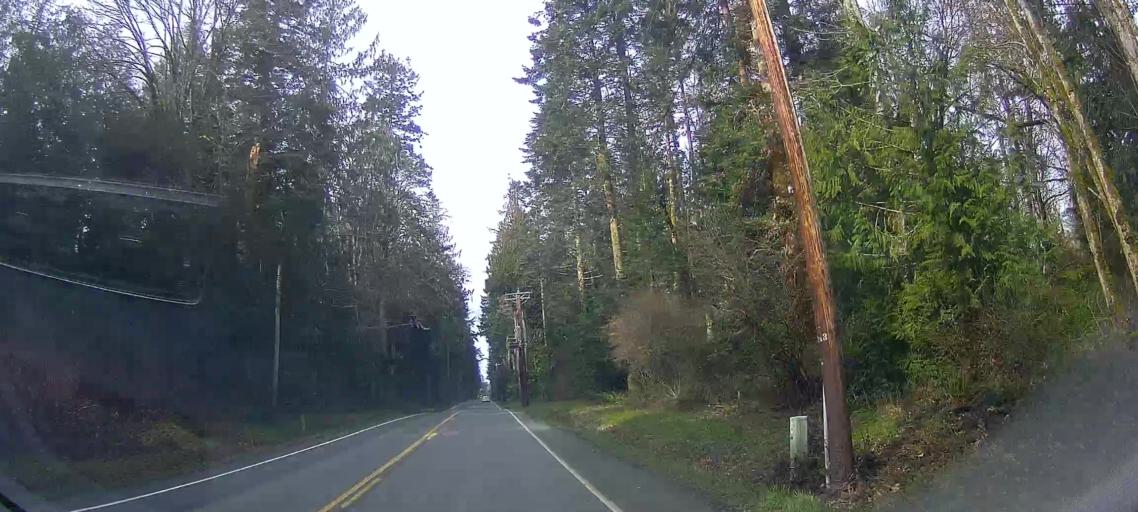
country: US
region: Washington
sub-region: Island County
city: Camano
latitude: 48.1241
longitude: -122.4550
